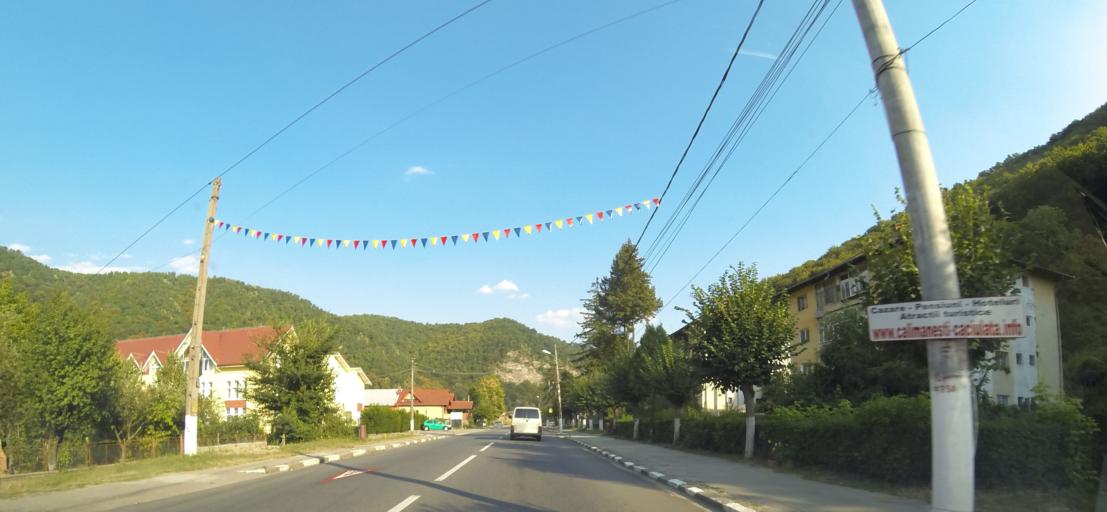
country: RO
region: Valcea
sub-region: Oras Calimanesti
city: Calimanesti
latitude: 45.2582
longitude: 24.3292
